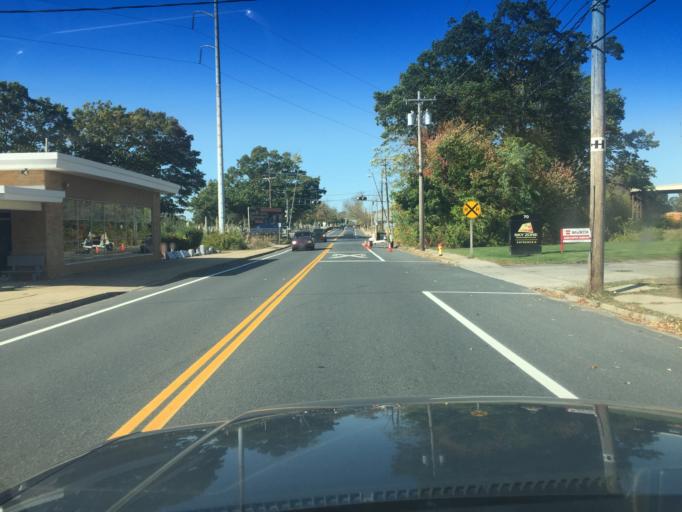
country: US
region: Rhode Island
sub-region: Providence County
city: Pawtucket
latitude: 41.8557
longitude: -71.3629
